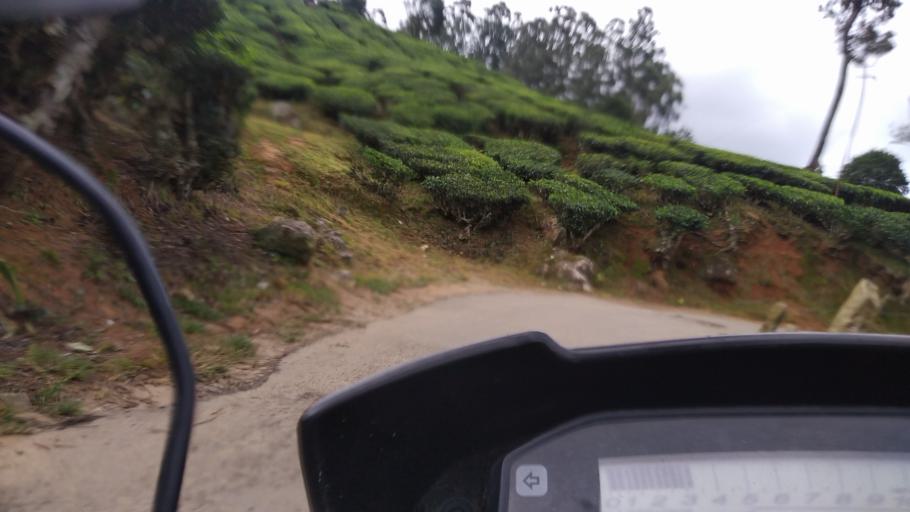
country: IN
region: Kerala
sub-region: Idukki
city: Munnar
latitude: 10.0333
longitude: 77.1680
